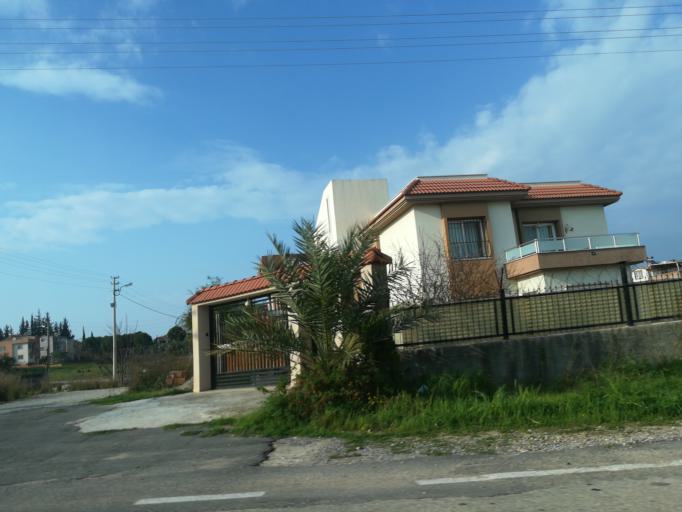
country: TR
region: Adana
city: Adana
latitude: 37.0779
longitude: 35.3911
